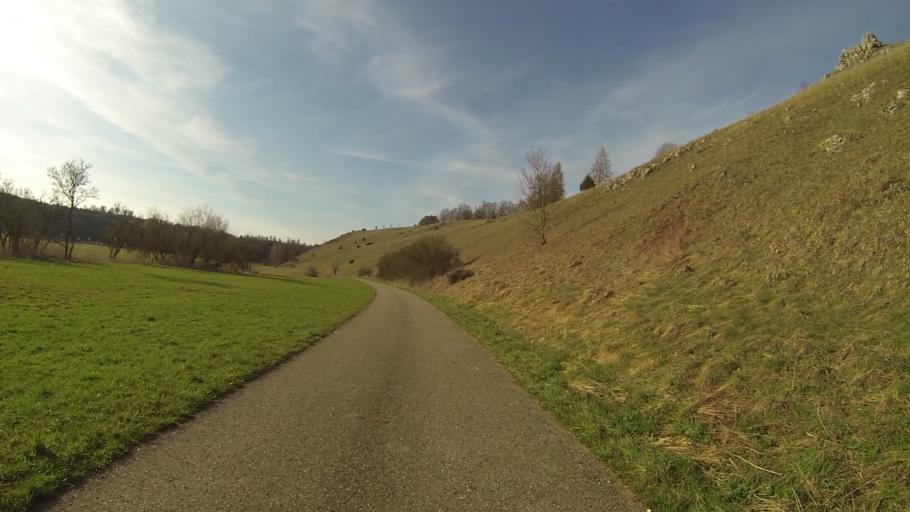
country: DE
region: Baden-Wuerttemberg
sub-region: Regierungsbezirk Stuttgart
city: Hermaringen
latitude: 48.5844
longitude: 10.2267
